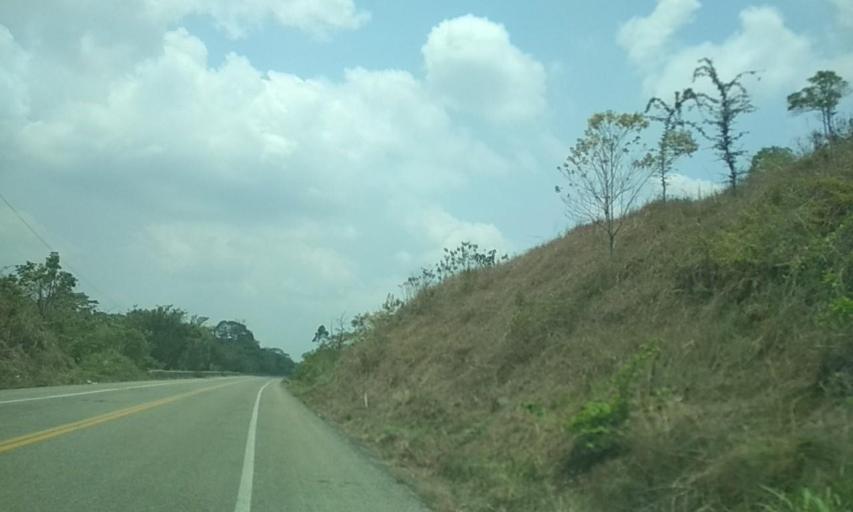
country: MX
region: Tabasco
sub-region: Huimanguillo
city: Francisco Rueda
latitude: 17.6483
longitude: -93.8333
